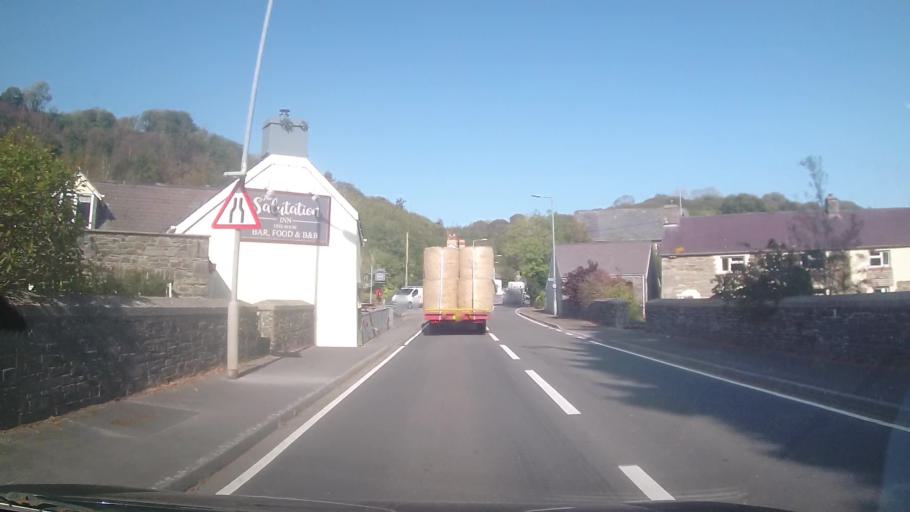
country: GB
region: Wales
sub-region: Pembrokeshire
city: Nevern
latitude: 52.0161
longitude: -4.7700
